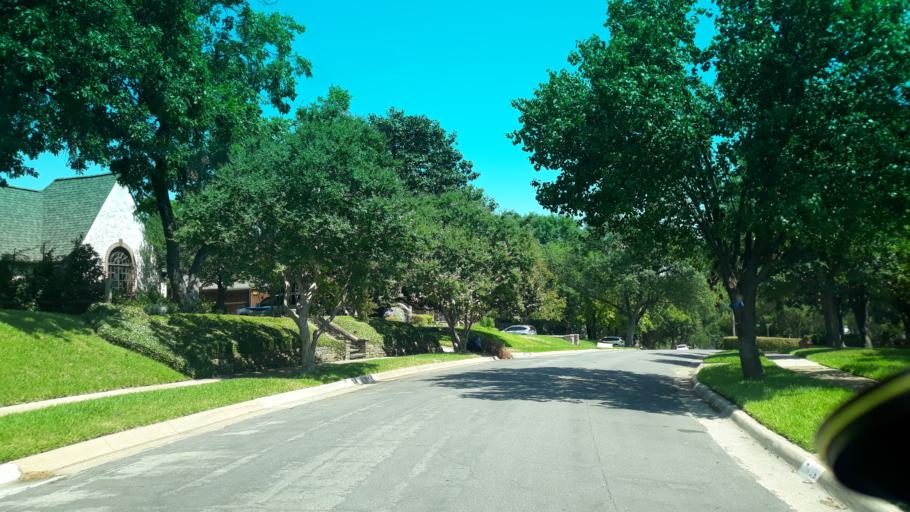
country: US
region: Texas
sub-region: Dallas County
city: Highland Park
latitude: 32.8165
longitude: -96.7400
